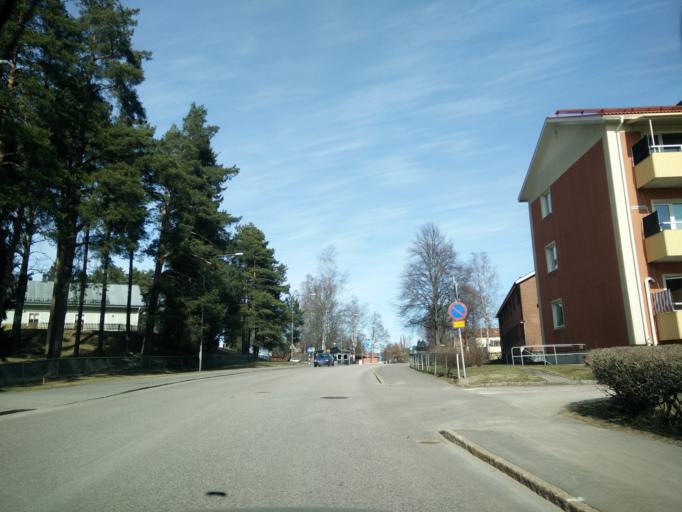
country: SE
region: Vaermland
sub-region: Hagfors Kommun
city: Hagfors
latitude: 60.0304
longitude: 13.6970
